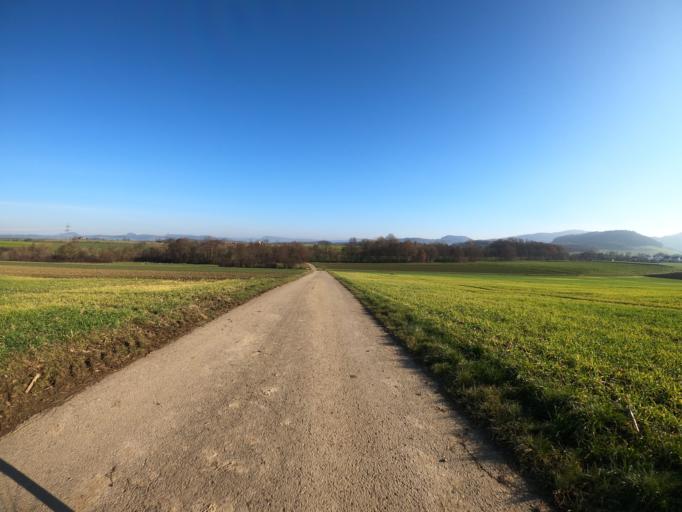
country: DE
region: Baden-Wuerttemberg
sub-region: Regierungsbezirk Stuttgart
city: Eschenbach
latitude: 48.6673
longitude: 9.6678
